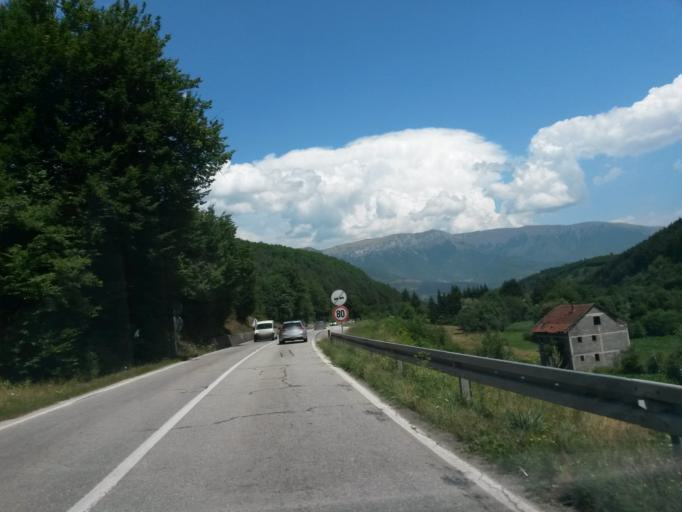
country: BA
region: Federation of Bosnia and Herzegovina
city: Turbe
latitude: 44.2230
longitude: 17.5469
